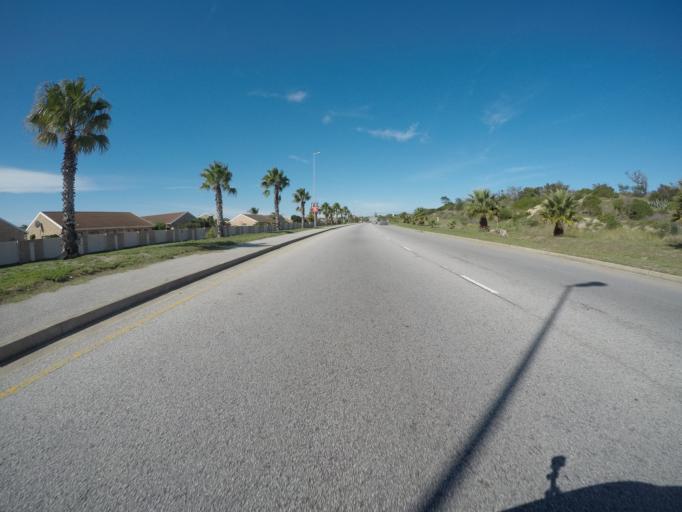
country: ZA
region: Eastern Cape
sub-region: Nelson Mandela Bay Metropolitan Municipality
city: Port Elizabeth
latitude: -33.9889
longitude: 25.6465
